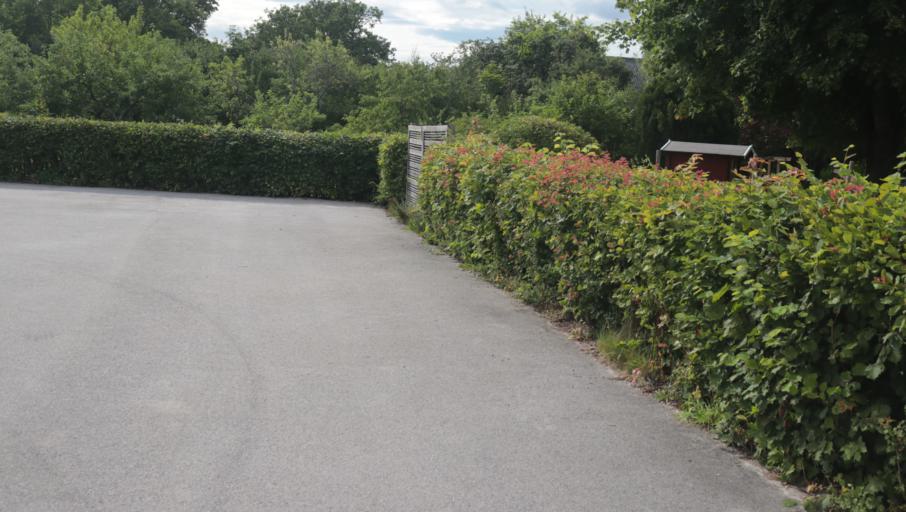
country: SE
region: Blekinge
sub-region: Karlshamns Kommun
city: Karlshamn
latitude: 56.2220
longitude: 14.8352
